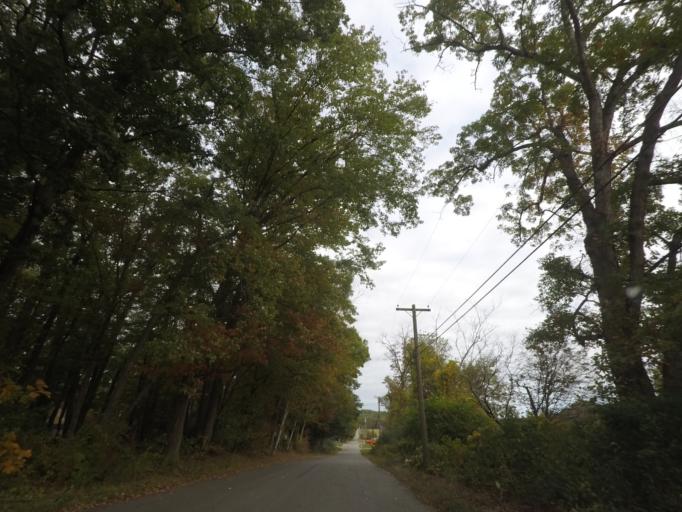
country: US
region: Connecticut
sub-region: Windham County
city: Thompson
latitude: 41.9552
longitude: -71.8338
